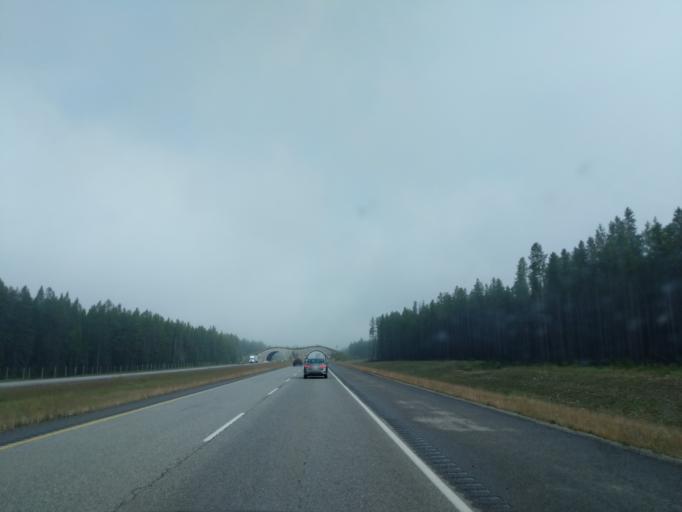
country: CA
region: Alberta
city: Lake Louise
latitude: 51.2714
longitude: -115.9530
